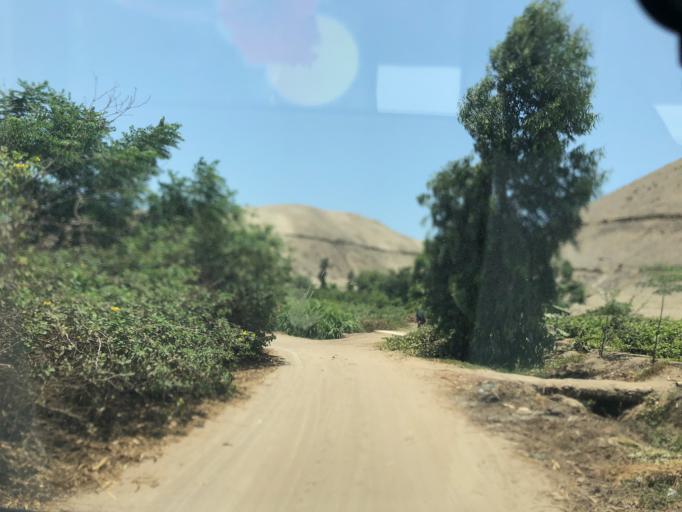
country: PE
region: Lima
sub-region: Provincia de Canete
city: Quilmana
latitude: -12.9921
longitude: -76.4382
